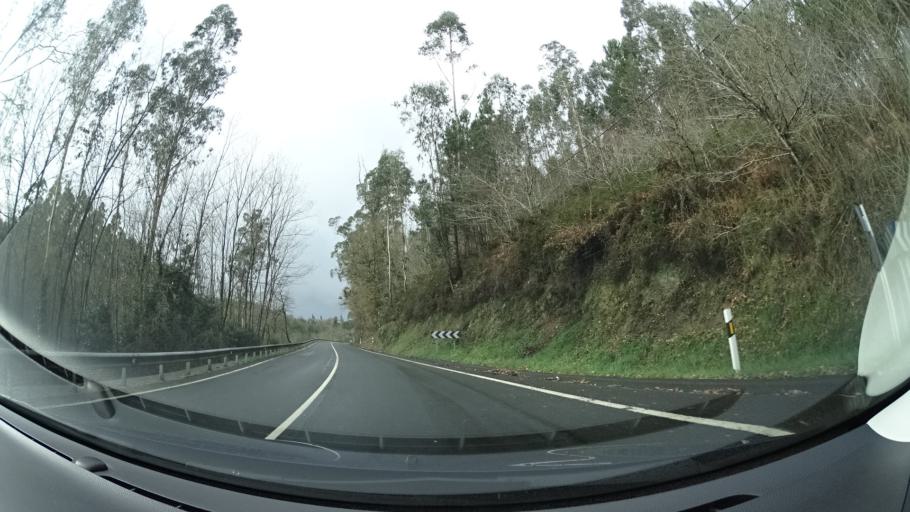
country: ES
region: Basque Country
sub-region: Bizkaia
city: Mungia
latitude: 43.3639
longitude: -2.8177
